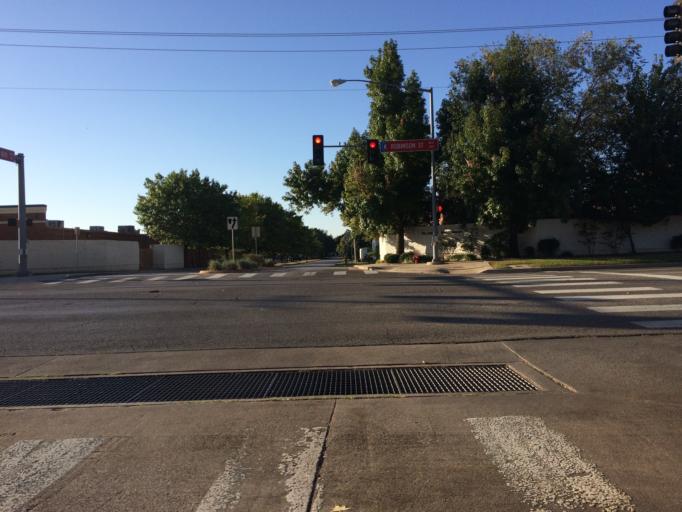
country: US
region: Oklahoma
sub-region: Cleveland County
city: Norman
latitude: 35.2331
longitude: -97.4972
